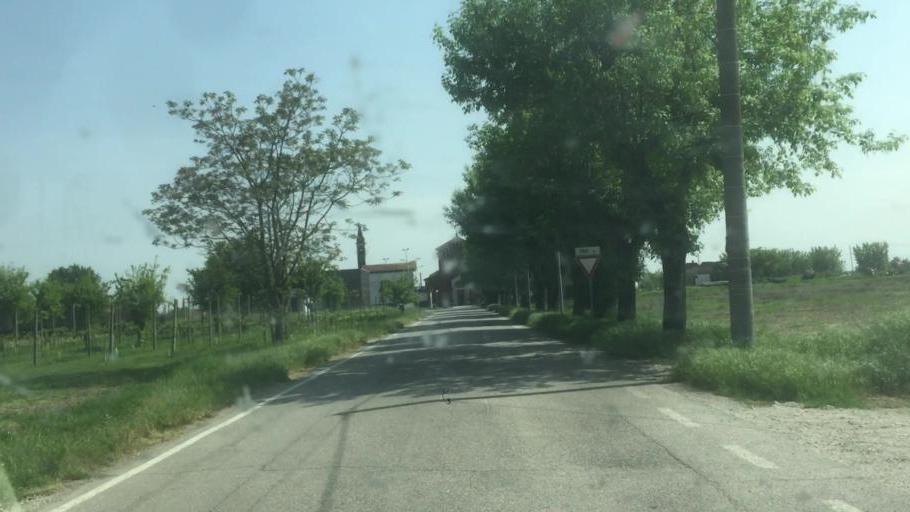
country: IT
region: Lombardy
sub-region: Provincia di Mantova
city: Commessaggio
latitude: 44.9992
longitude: 10.5866
